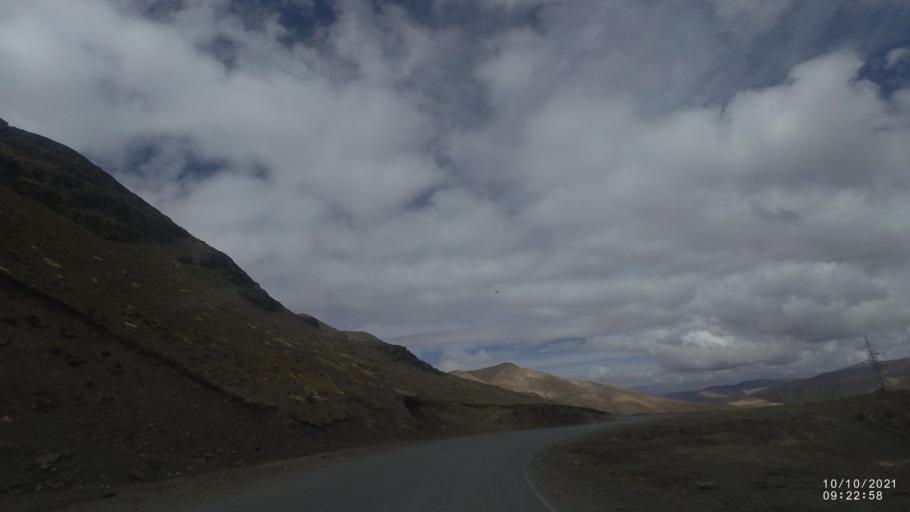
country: BO
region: La Paz
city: Quime
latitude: -17.0817
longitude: -67.2996
